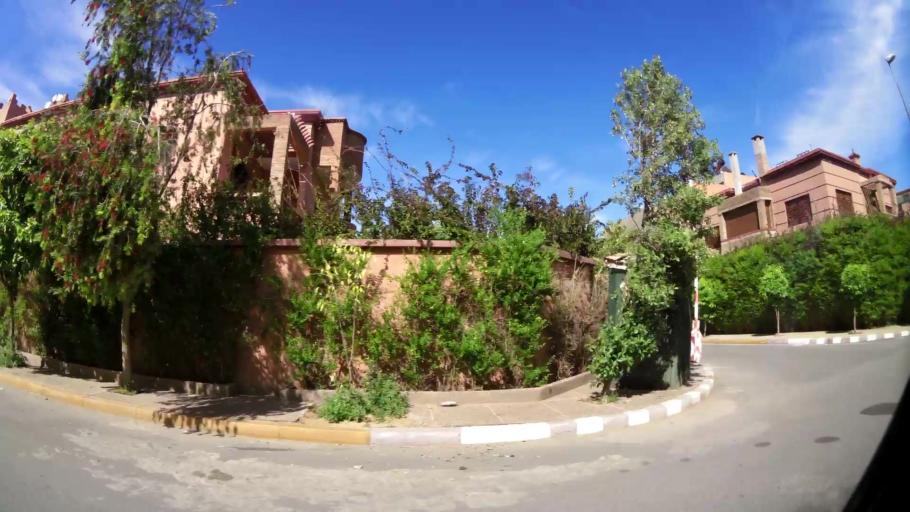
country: MA
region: Marrakech-Tensift-Al Haouz
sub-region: Marrakech
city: Marrakesh
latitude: 31.6643
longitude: -8.0287
